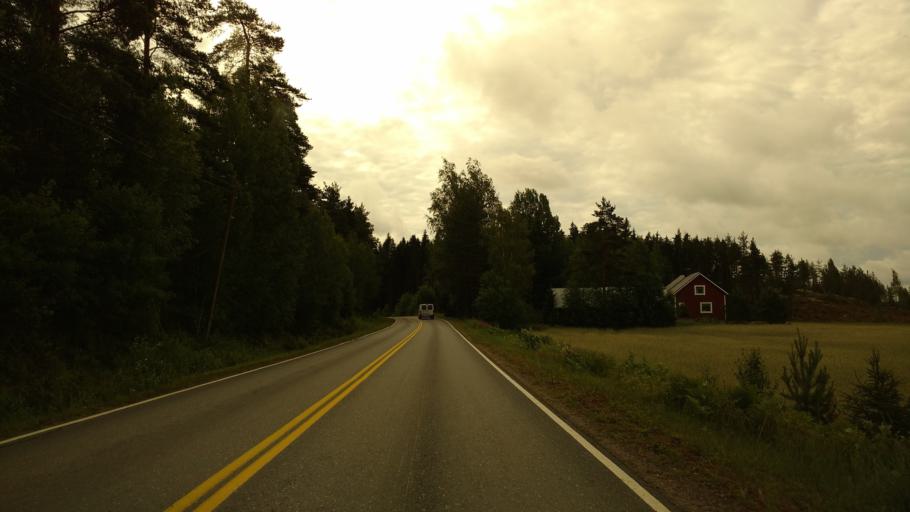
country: FI
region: Varsinais-Suomi
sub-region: Salo
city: Kuusjoki
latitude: 60.5534
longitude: 23.1574
